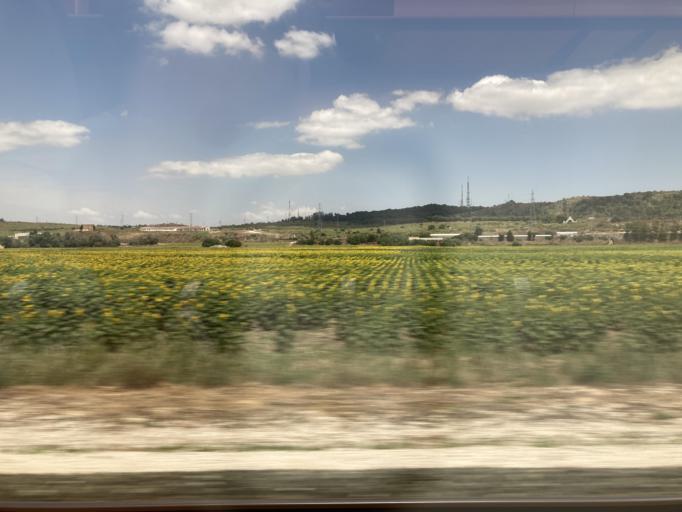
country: ES
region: Andalusia
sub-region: Provincia de Cadiz
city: Jerez de la Frontera
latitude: 36.6203
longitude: -6.1564
